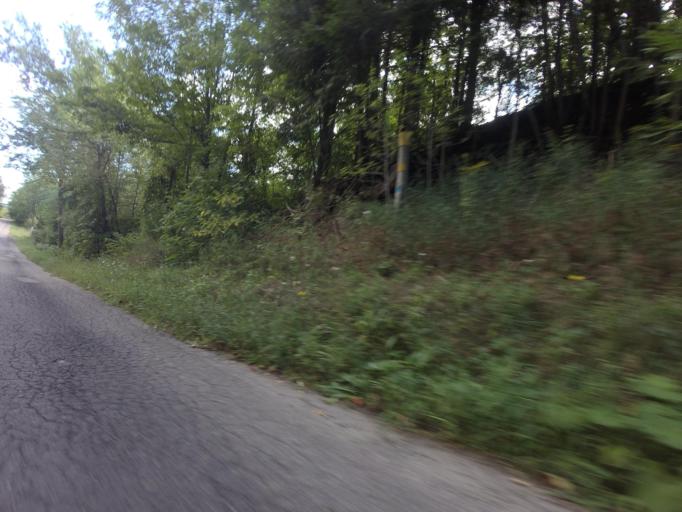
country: CA
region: Ontario
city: Orangeville
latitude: 43.8190
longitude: -79.9885
